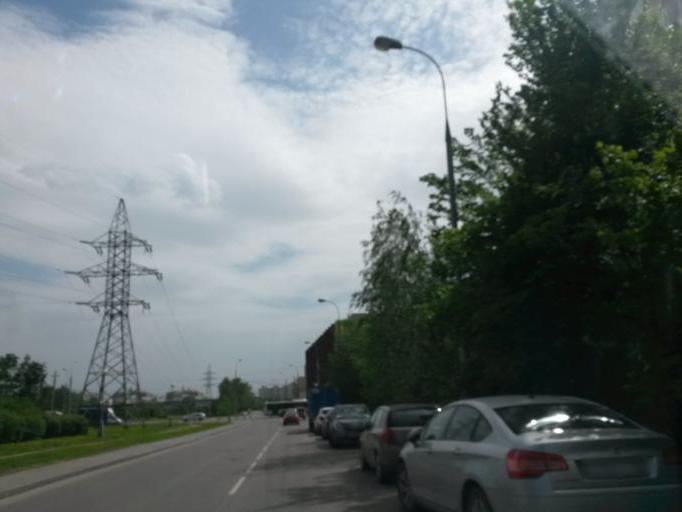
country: RU
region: Moskovskaya
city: Kommunarka
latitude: 55.5456
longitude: 37.5244
